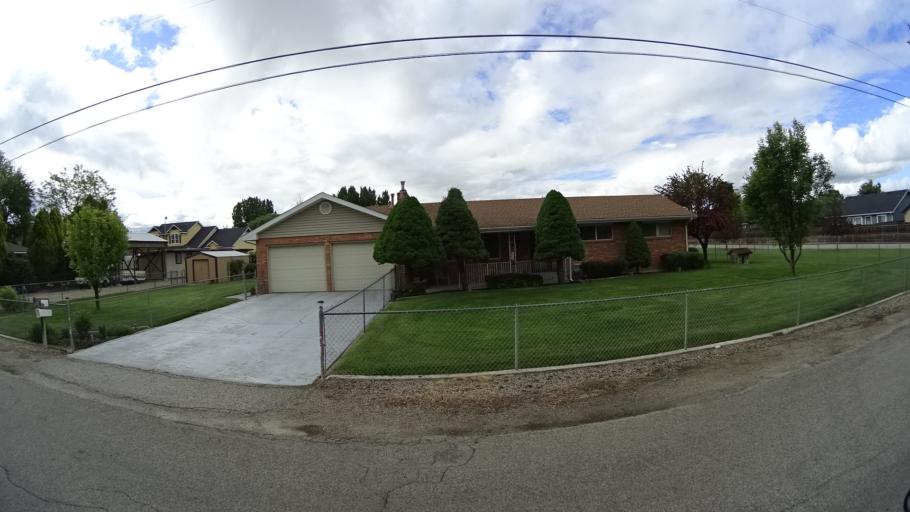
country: US
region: Idaho
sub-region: Ada County
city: Garden City
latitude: 43.6720
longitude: -116.2711
